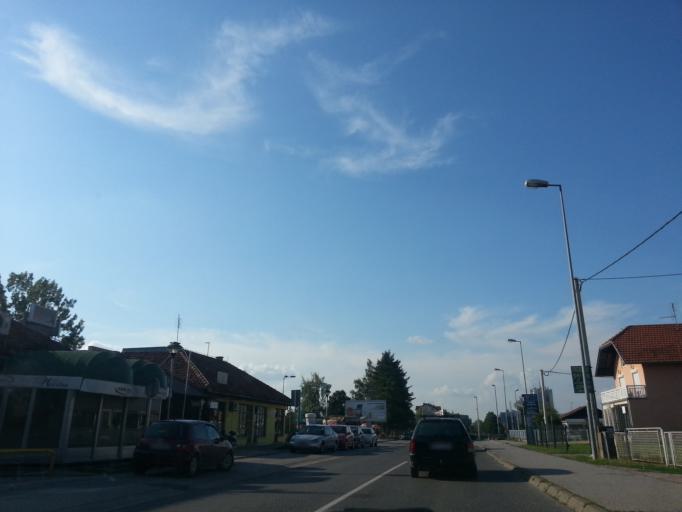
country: BA
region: Brcko
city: Brcko
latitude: 44.8632
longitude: 18.8116
